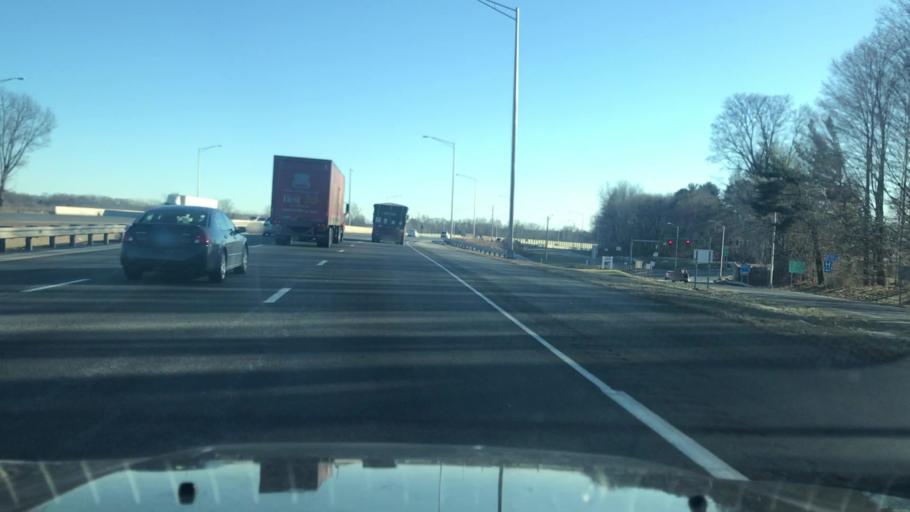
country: US
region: Connecticut
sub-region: New Haven County
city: Cheshire Village
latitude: 41.5880
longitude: -72.9005
